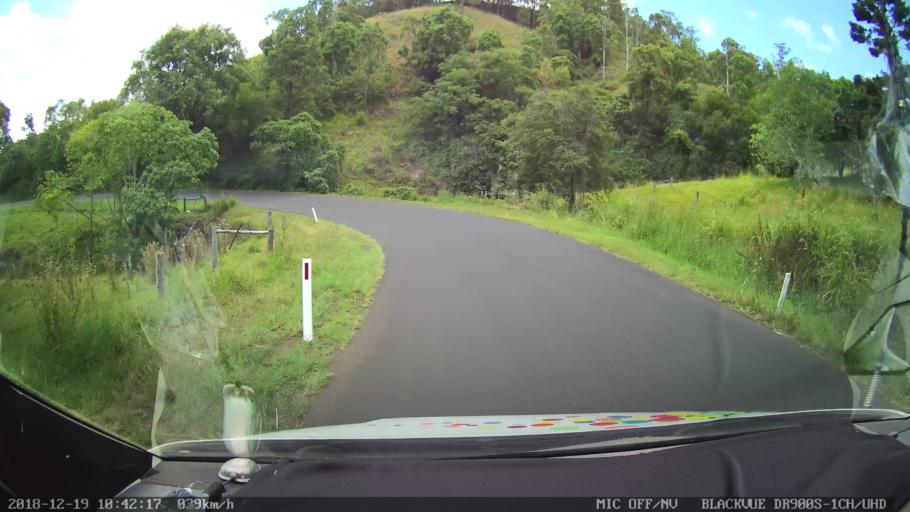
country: AU
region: New South Wales
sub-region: Lismore Municipality
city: Nimbin
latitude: -28.5920
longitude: 153.1666
